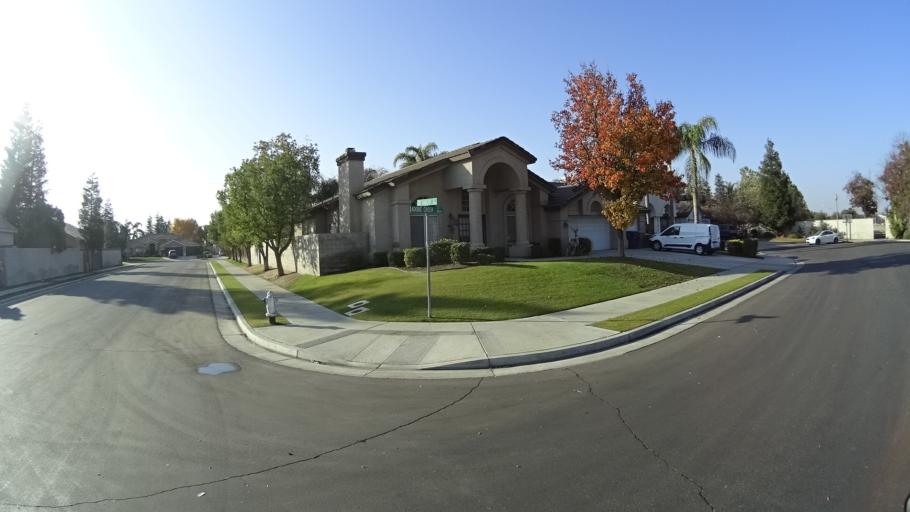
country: US
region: California
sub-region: Kern County
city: Greenacres
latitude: 35.3657
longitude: -119.1249
